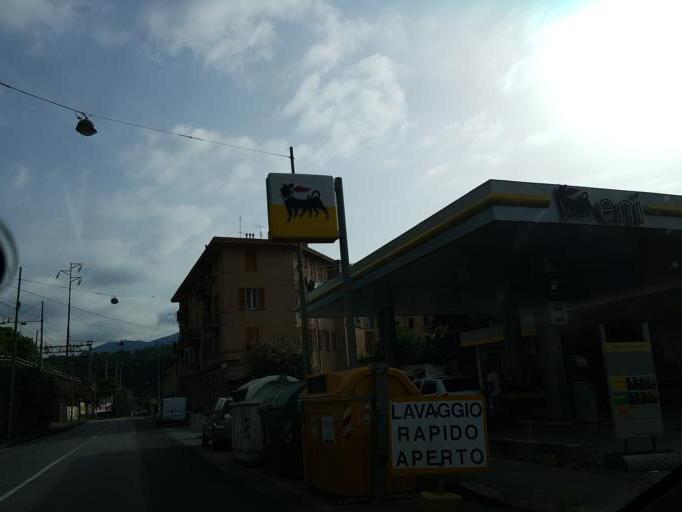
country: IT
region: Liguria
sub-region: Provincia di Genova
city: Santa Marta
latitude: 44.4898
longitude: 8.9020
